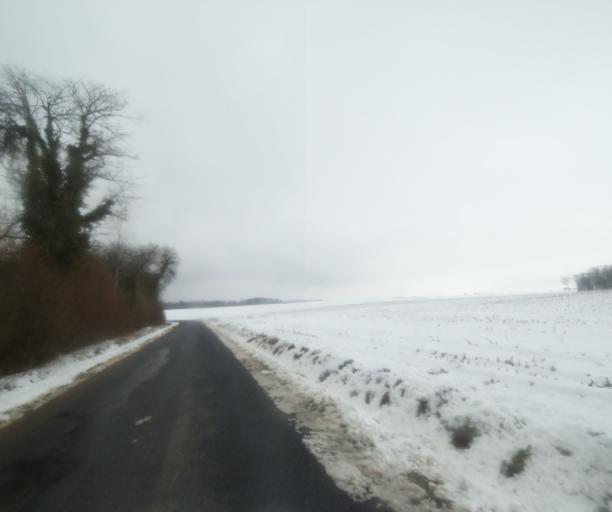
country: FR
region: Champagne-Ardenne
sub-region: Departement de la Haute-Marne
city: Montier-en-Der
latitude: 48.4660
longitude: 4.8174
